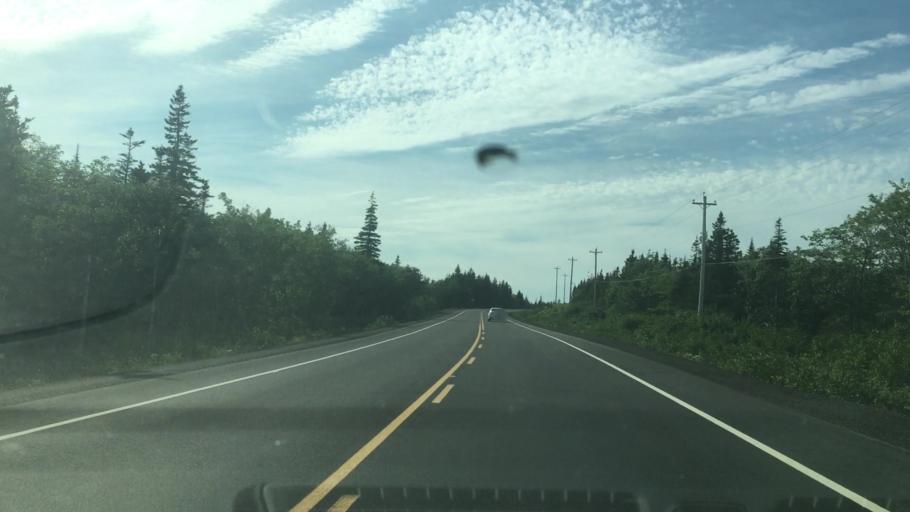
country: CA
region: Nova Scotia
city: Sydney Mines
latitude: 46.8428
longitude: -60.3990
